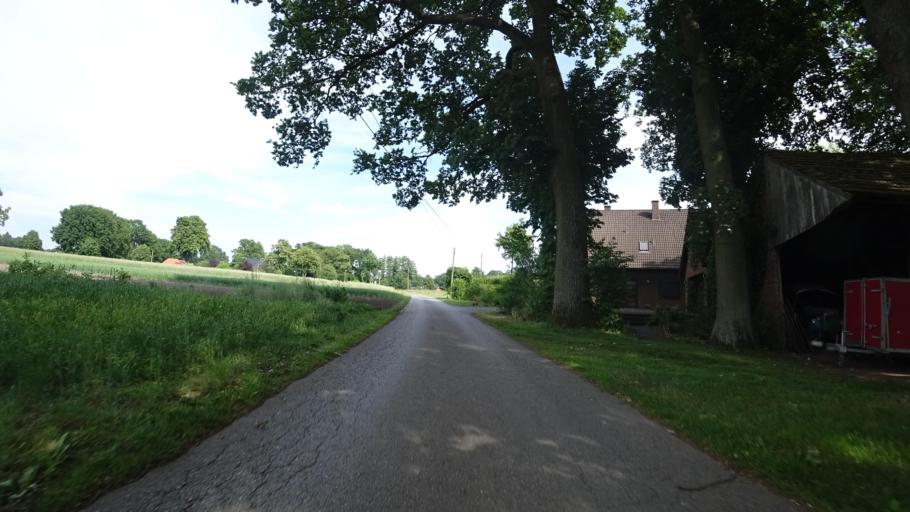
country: DE
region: North Rhine-Westphalia
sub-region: Regierungsbezirk Detmold
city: Verl
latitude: 51.9029
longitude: 8.4640
